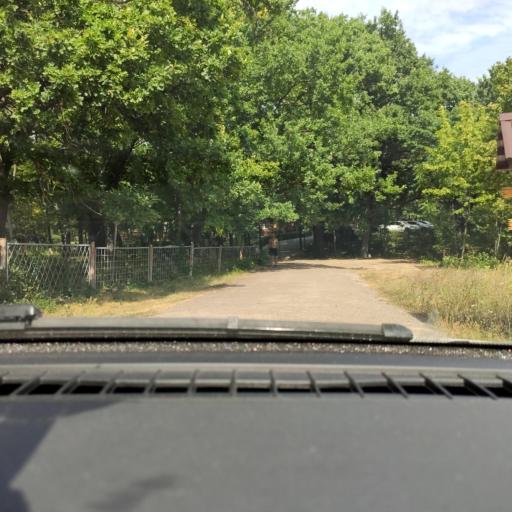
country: RU
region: Voronezj
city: Pridonskoy
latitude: 51.7568
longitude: 39.0794
